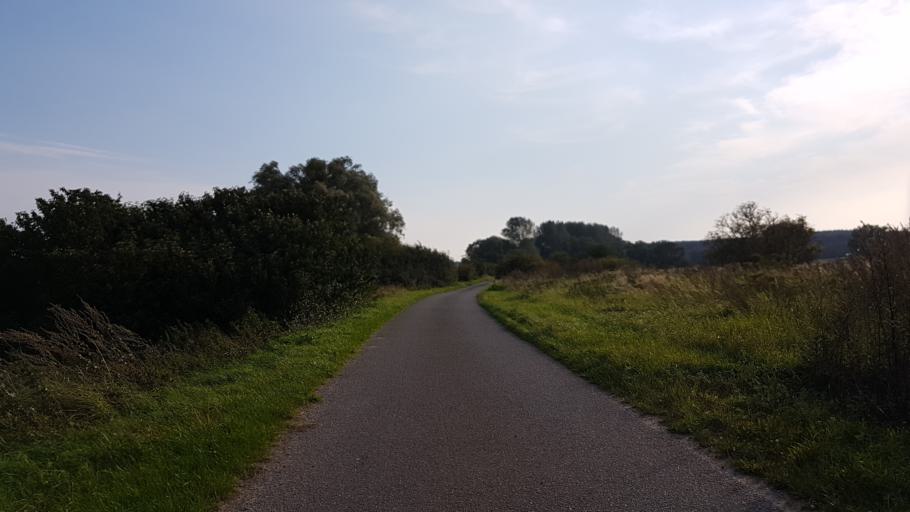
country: DE
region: Mecklenburg-Vorpommern
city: Sagard
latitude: 54.5141
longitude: 13.5300
